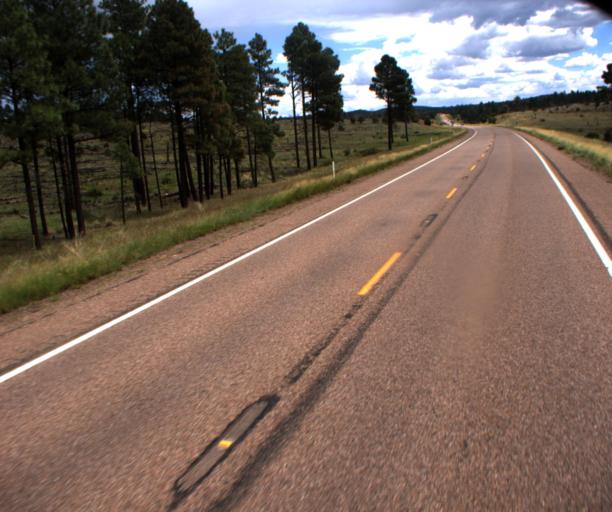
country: US
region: Arizona
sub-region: Navajo County
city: Linden
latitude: 34.3125
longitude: -110.2362
